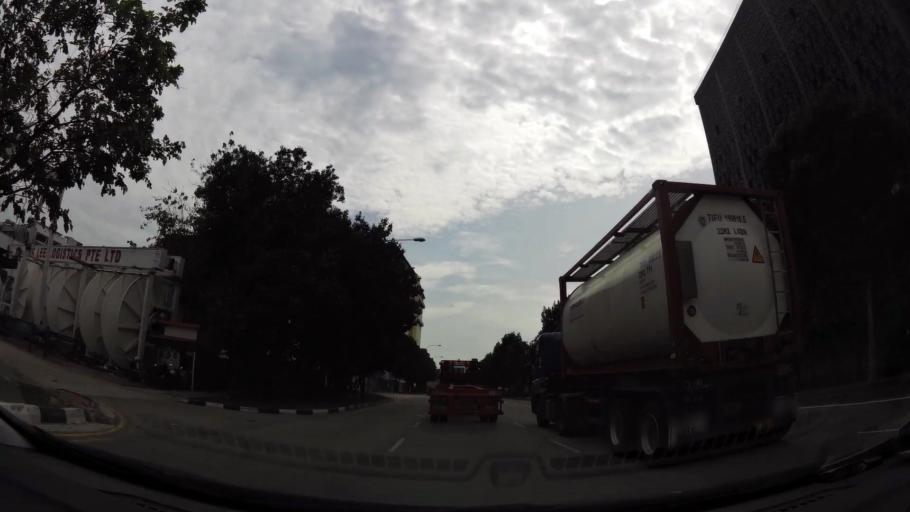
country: SG
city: Singapore
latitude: 1.3140
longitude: 103.7214
